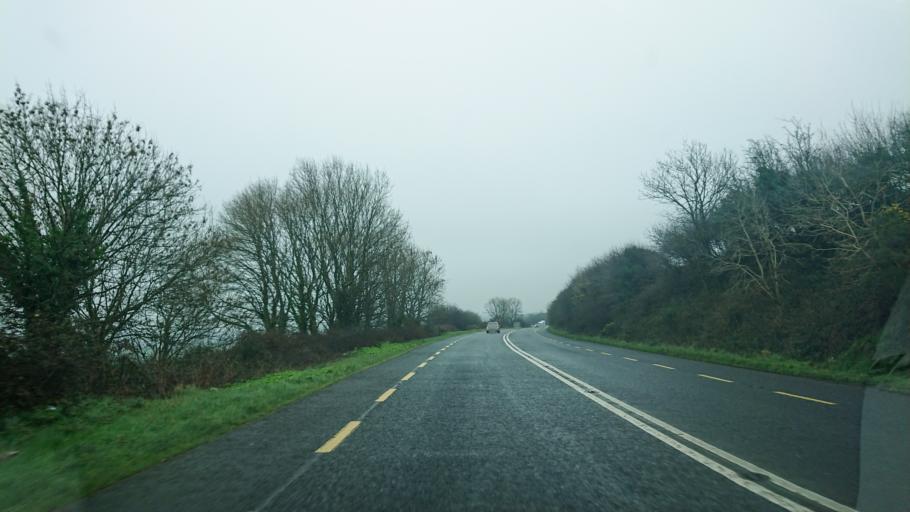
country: IE
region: Munster
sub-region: County Cork
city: Killumney
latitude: 51.7860
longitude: -8.6282
